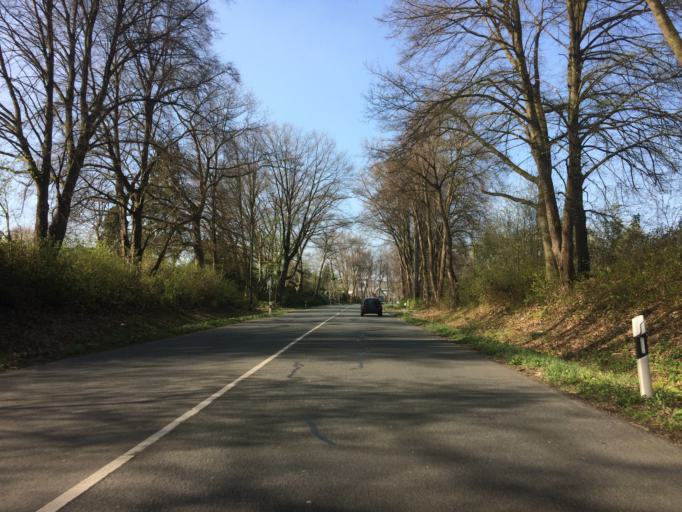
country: DE
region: North Rhine-Westphalia
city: Hattingen
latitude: 51.4188
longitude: 7.1698
